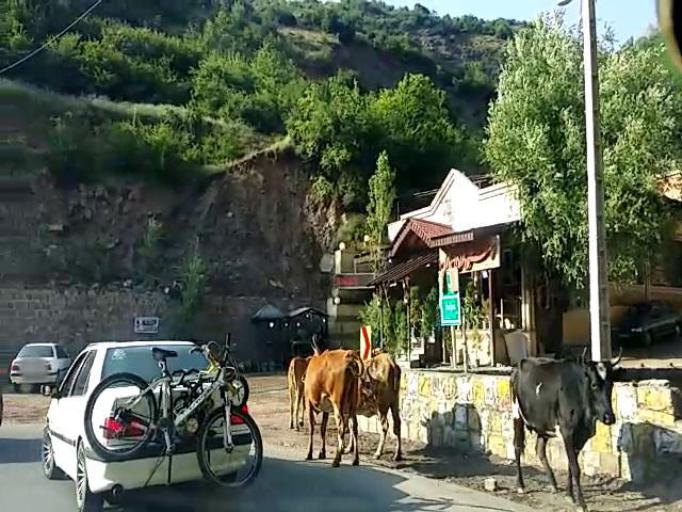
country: IR
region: Mazandaran
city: Chalus
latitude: 36.2323
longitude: 51.3154
